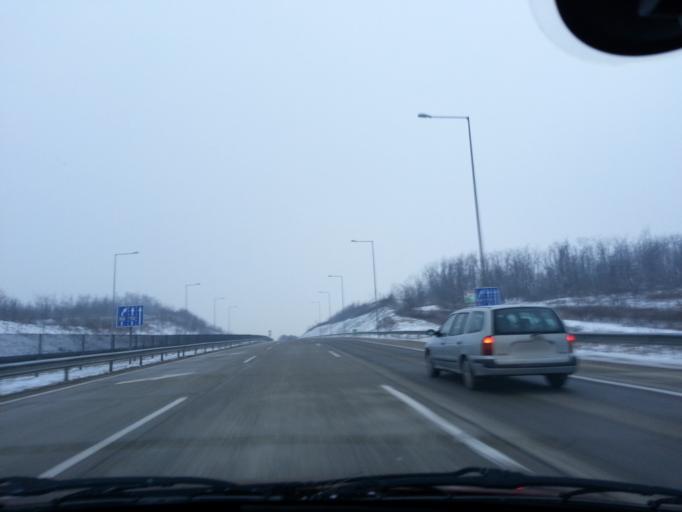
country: HU
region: Pest
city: Kerepes
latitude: 47.5656
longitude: 19.3229
